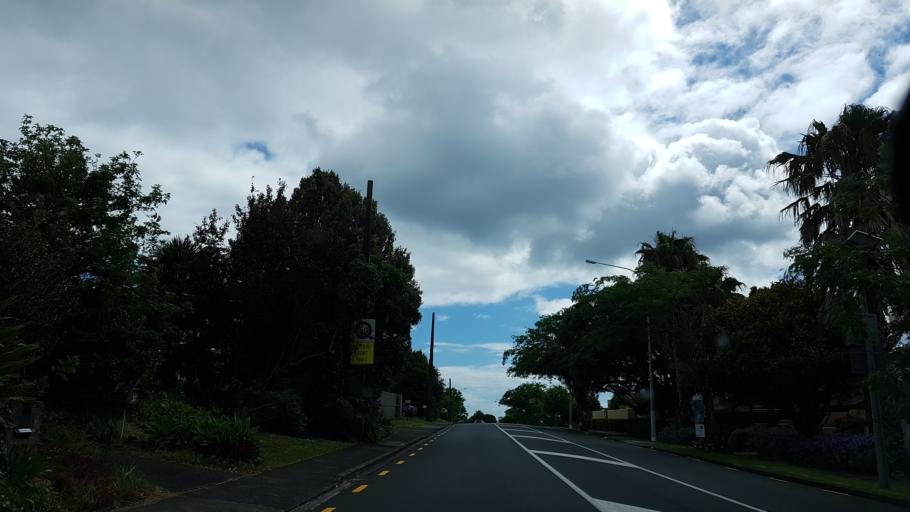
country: NZ
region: Auckland
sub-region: Auckland
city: North Shore
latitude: -36.7855
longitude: 174.7694
